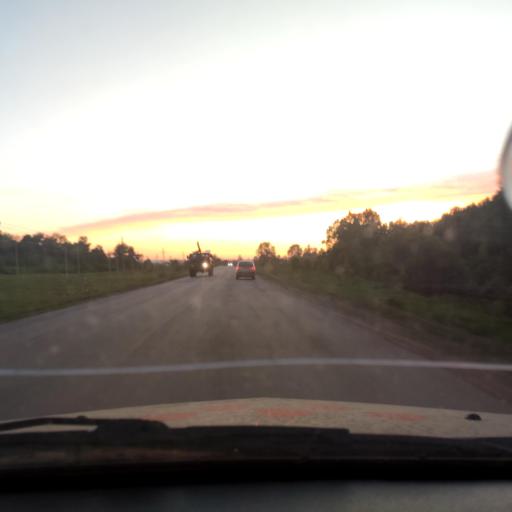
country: RU
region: Bashkortostan
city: Iglino
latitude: 54.7426
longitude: 56.2232
